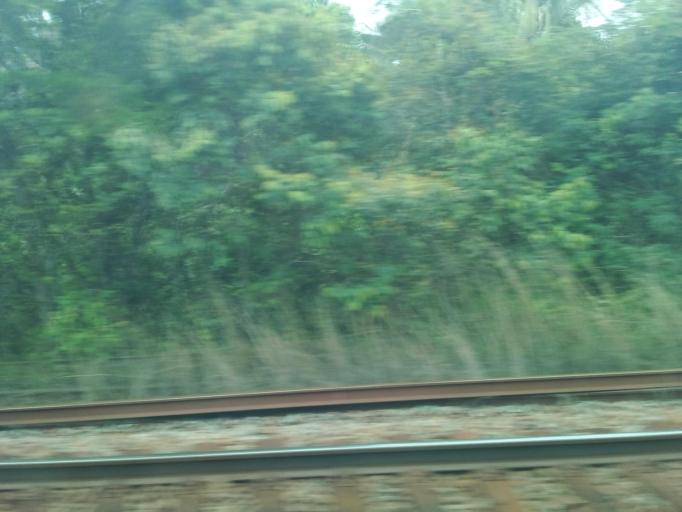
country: BR
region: Maranhao
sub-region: Santa Ines
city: Santa Ines
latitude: -3.6525
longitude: -45.7988
